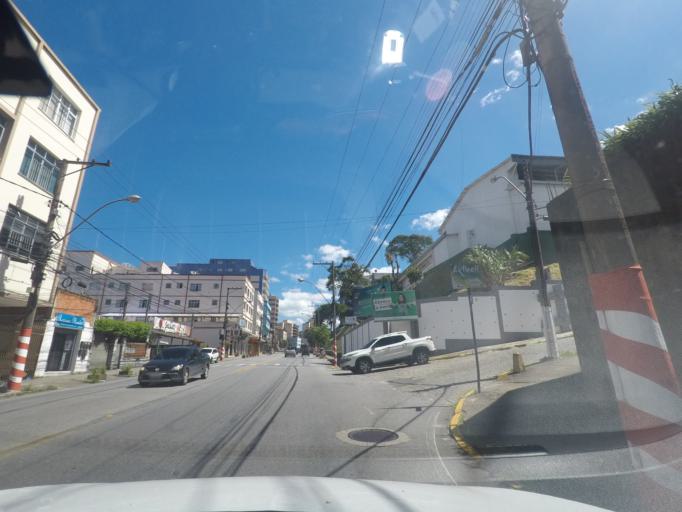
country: BR
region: Rio de Janeiro
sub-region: Teresopolis
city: Teresopolis
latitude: -22.4329
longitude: -42.9787
